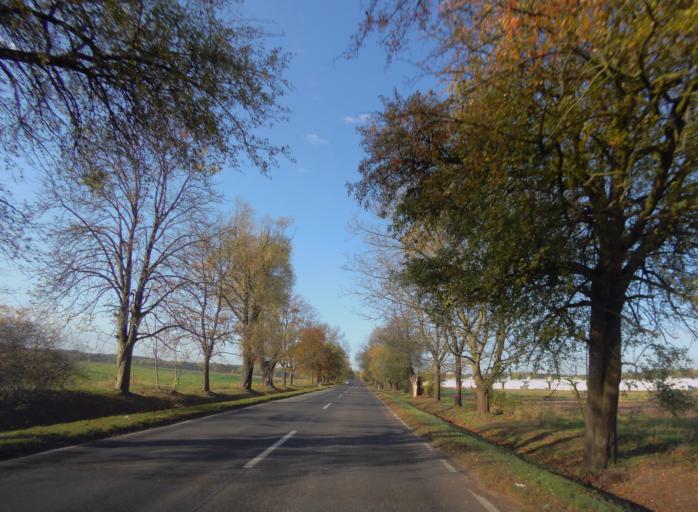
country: PL
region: Masovian Voivodeship
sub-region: Powiat siedlecki
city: Mordy
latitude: 52.1998
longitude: 22.4952
